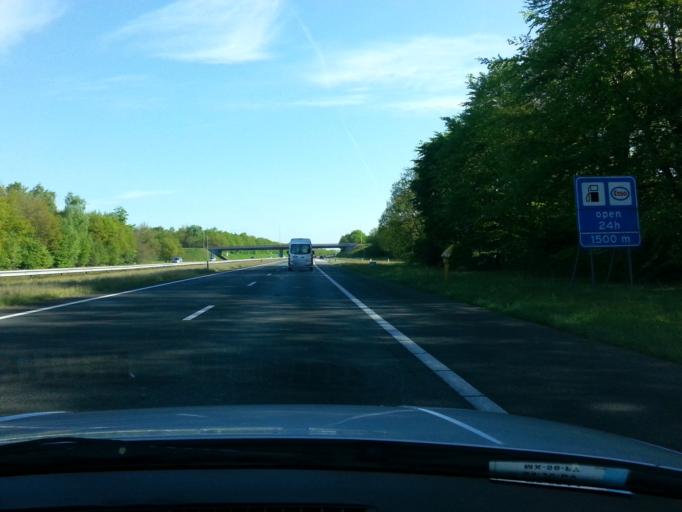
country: NL
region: North Holland
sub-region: Gemeente Laren
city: Laren
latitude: 52.2478
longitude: 5.2473
